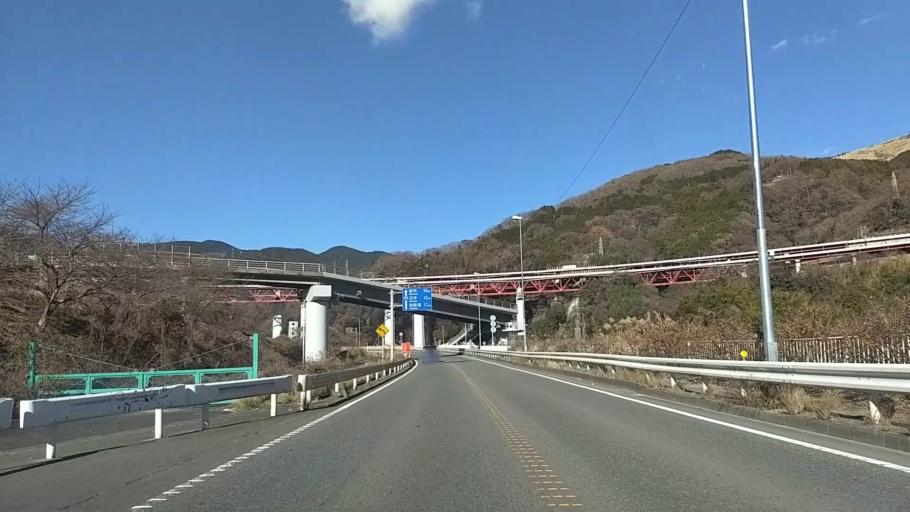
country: JP
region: Shizuoka
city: Gotemba
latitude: 35.3662
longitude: 139.0388
